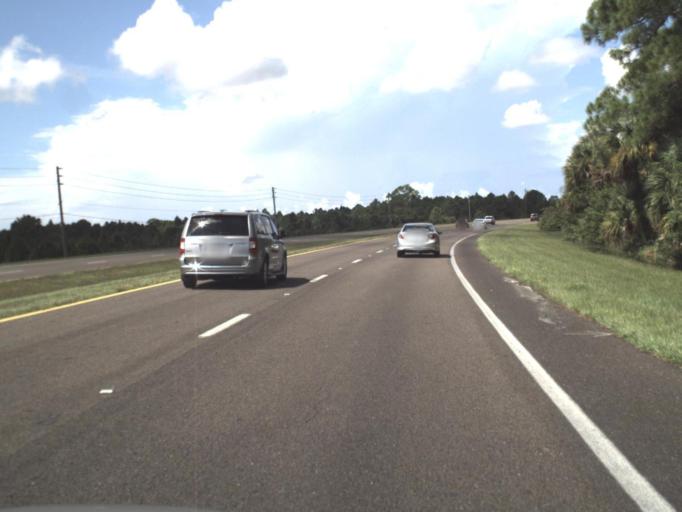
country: US
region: Florida
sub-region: Sarasota County
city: Warm Mineral Springs
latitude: 27.0421
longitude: -82.3040
